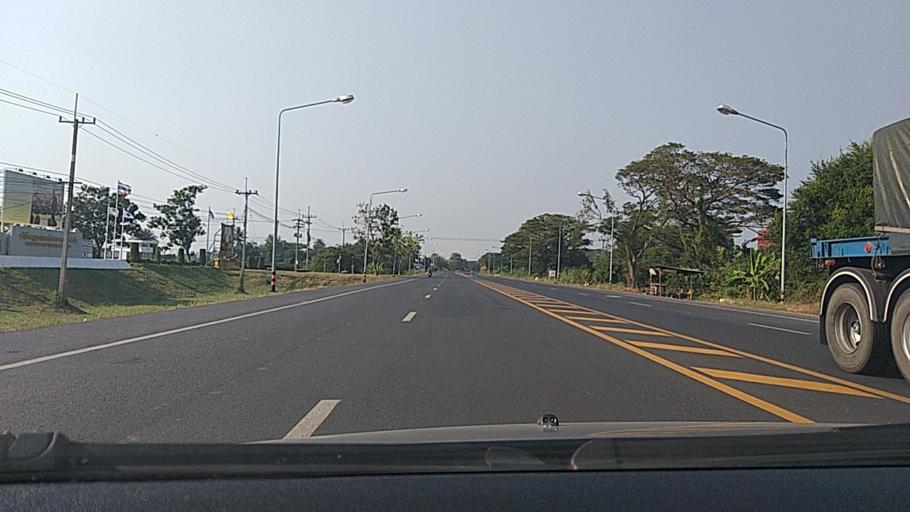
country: TH
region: Sing Buri
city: Phrom Buri
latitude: 14.7755
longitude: 100.4359
